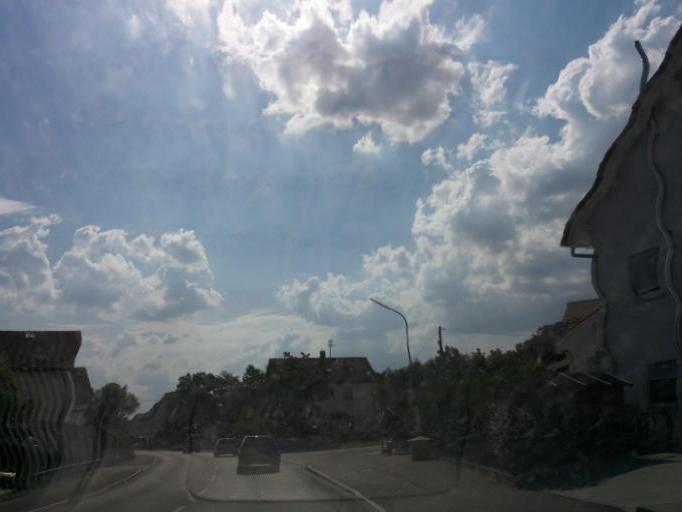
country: DE
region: Bavaria
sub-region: Upper Bavaria
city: Lenting
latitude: 48.7935
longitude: 11.4410
